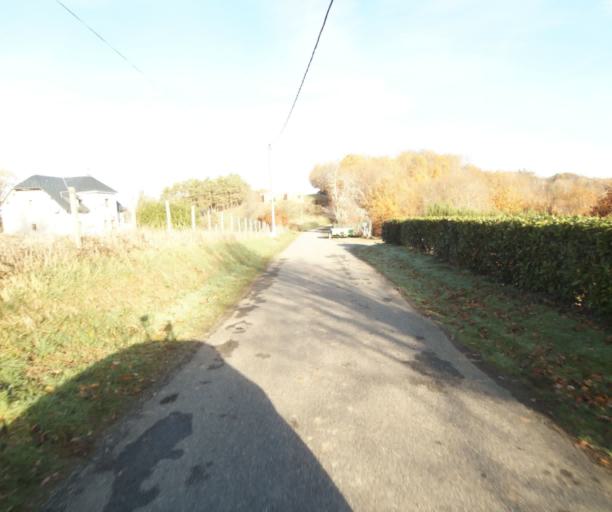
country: FR
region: Limousin
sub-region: Departement de la Correze
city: Laguenne
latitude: 45.2579
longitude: 1.7989
